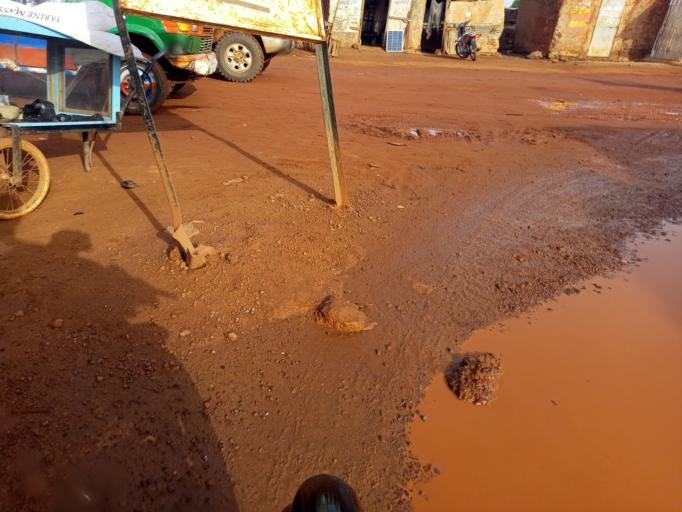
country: ML
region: Bamako
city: Bamako
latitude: 12.5223
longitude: -7.9947
